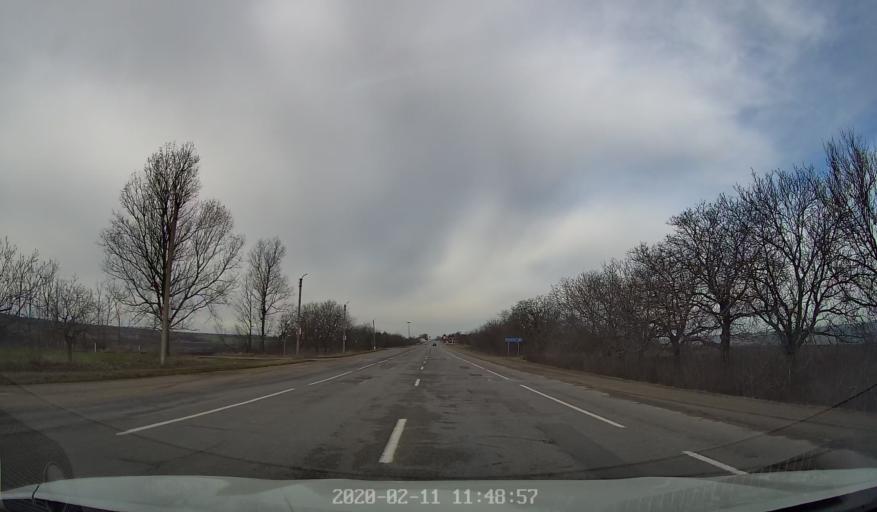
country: MD
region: Balti
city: Balti
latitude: 47.8440
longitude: 27.7969
